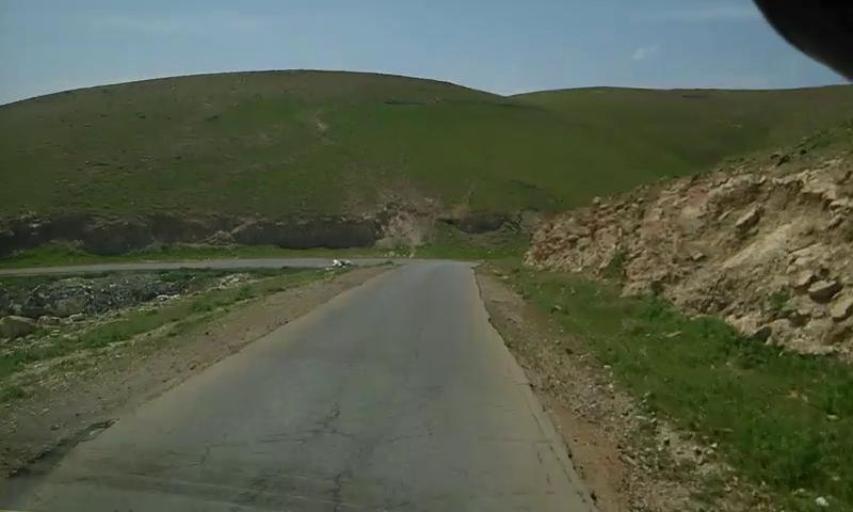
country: PS
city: `Arab ar Rashaydah
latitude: 31.5562
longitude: 35.2476
